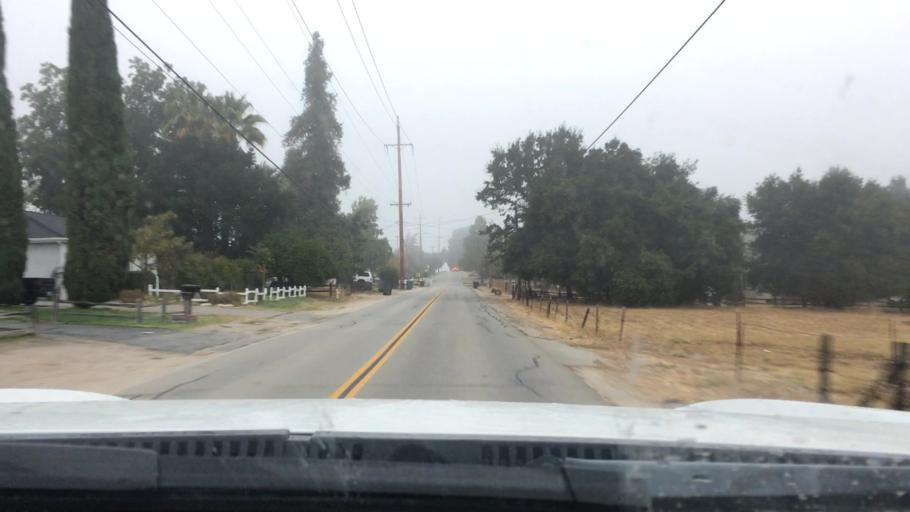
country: US
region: California
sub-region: San Luis Obispo County
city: Atascadero
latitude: 35.4868
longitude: -120.6856
